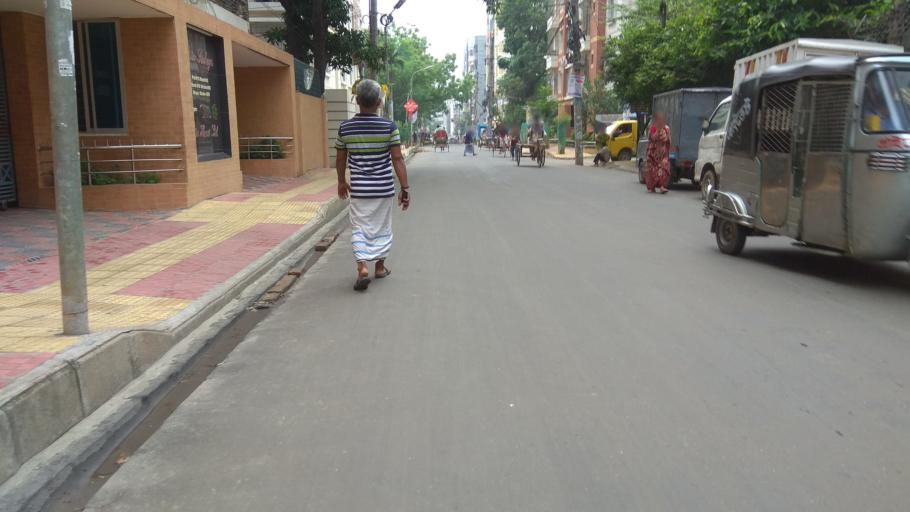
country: BD
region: Dhaka
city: Azimpur
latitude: 23.8053
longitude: 90.3571
